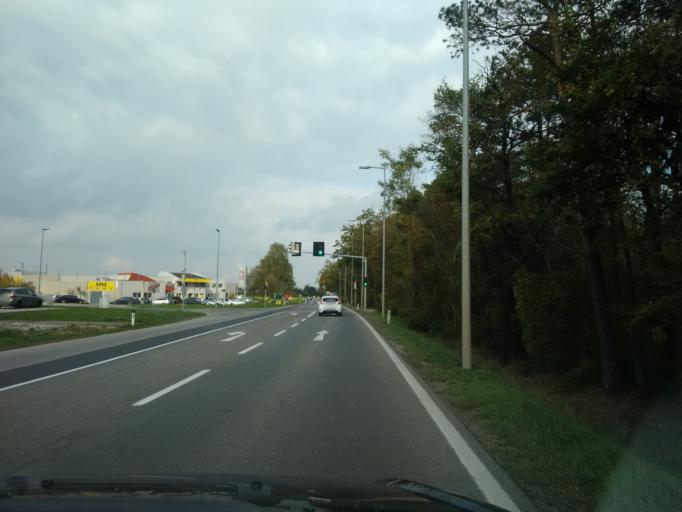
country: AT
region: Upper Austria
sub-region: Wels-Land
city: Gunskirchen
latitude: 48.1343
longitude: 13.9624
